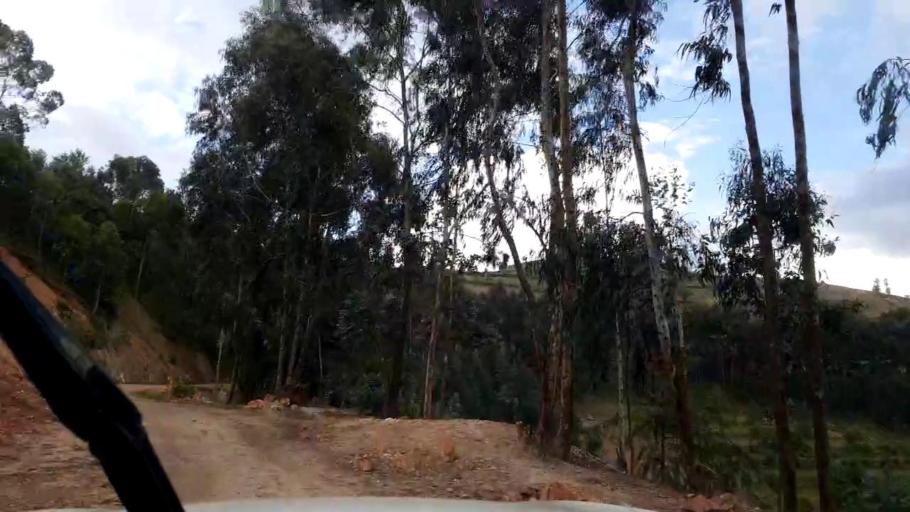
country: RW
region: Southern Province
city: Gitarama
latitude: -1.8660
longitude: 29.5698
